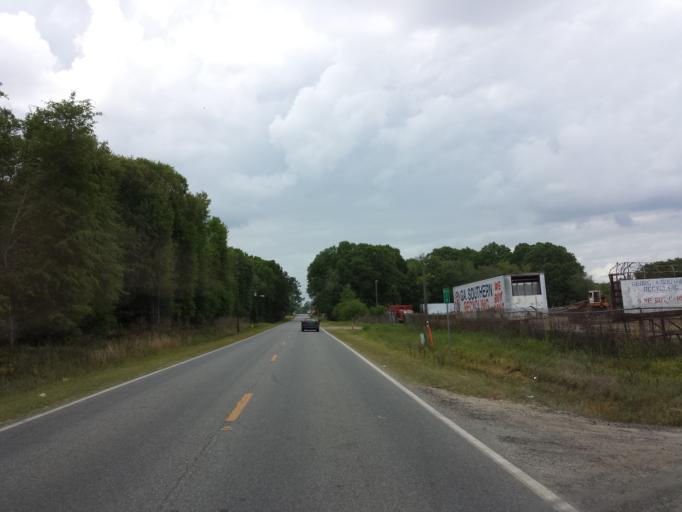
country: US
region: Georgia
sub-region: Cook County
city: Sparks
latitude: 31.2653
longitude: -83.4635
